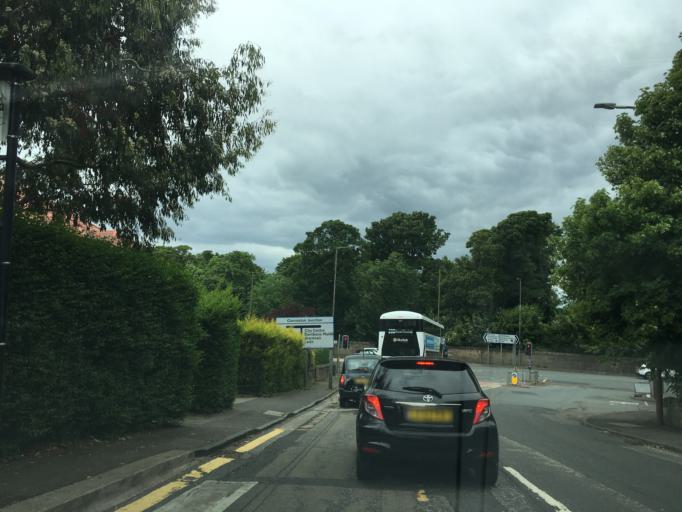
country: GB
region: Scotland
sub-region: Edinburgh
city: Colinton
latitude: 55.9615
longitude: -3.2824
